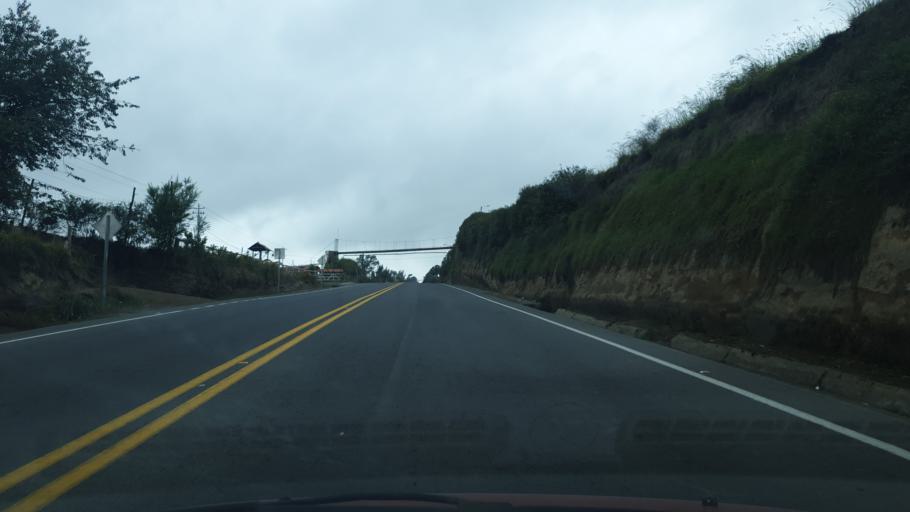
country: EC
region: Tungurahua
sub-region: Canton Quero
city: Quero
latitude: -1.3709
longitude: -78.6518
